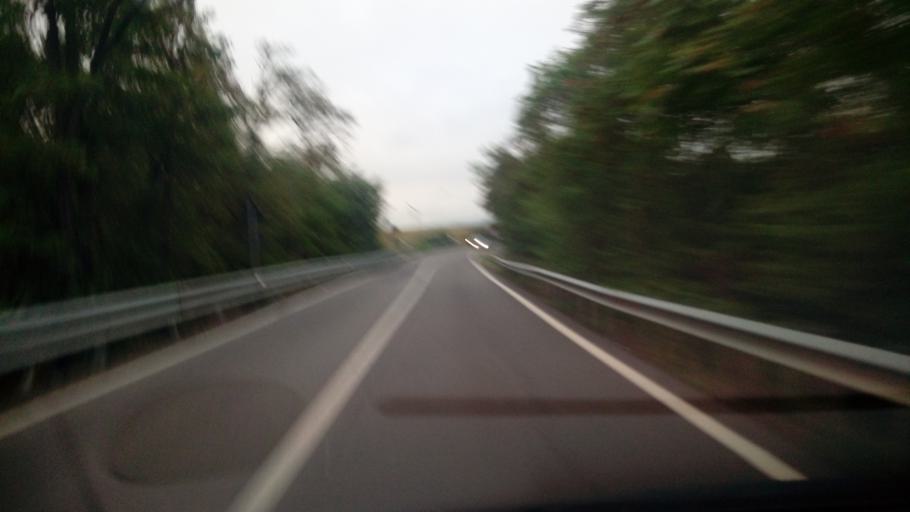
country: IT
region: Emilia-Romagna
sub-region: Provincia di Reggio Emilia
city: Pratissolo
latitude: 44.6186
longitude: 10.6730
